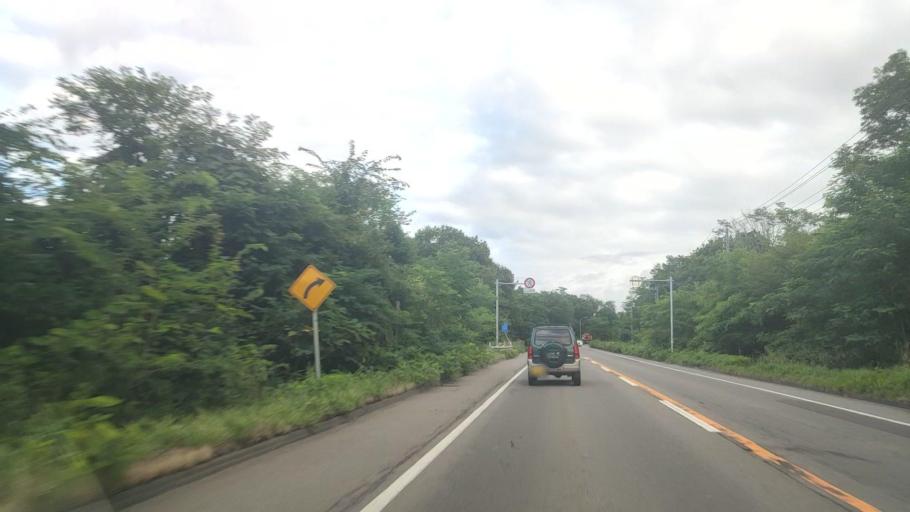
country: JP
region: Hokkaido
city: Nanae
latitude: 42.0738
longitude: 140.6015
